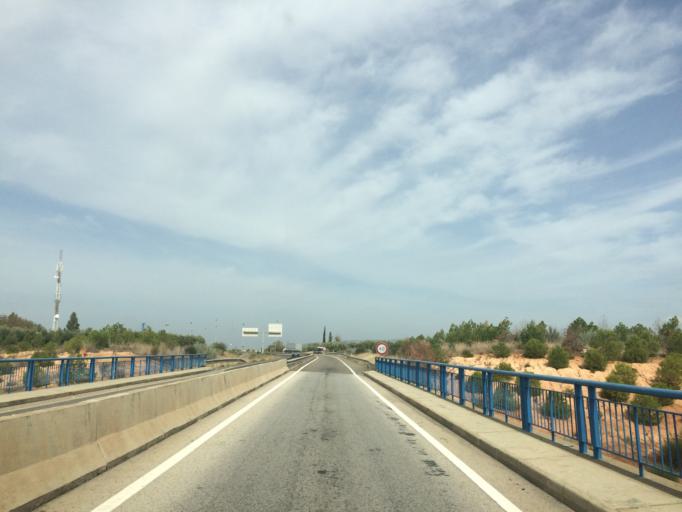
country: MA
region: Meknes-Tafilalet
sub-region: Meknes
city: Meknes
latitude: 33.8304
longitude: -5.5138
